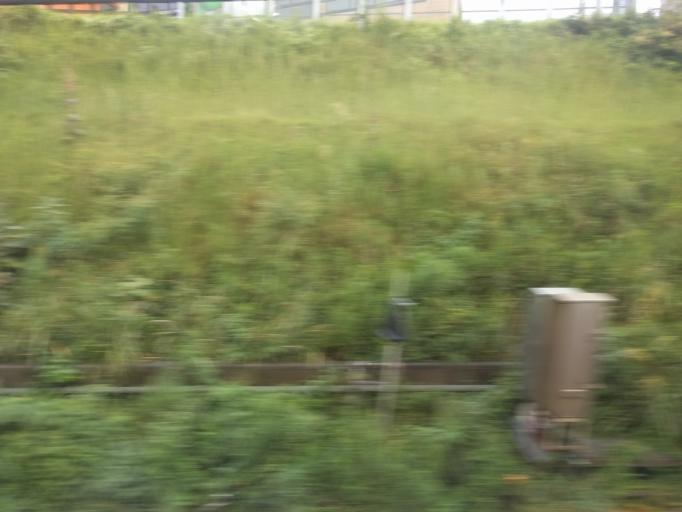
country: JP
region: Tokyo
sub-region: Machida-shi
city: Machida
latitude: 35.5125
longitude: 139.4752
